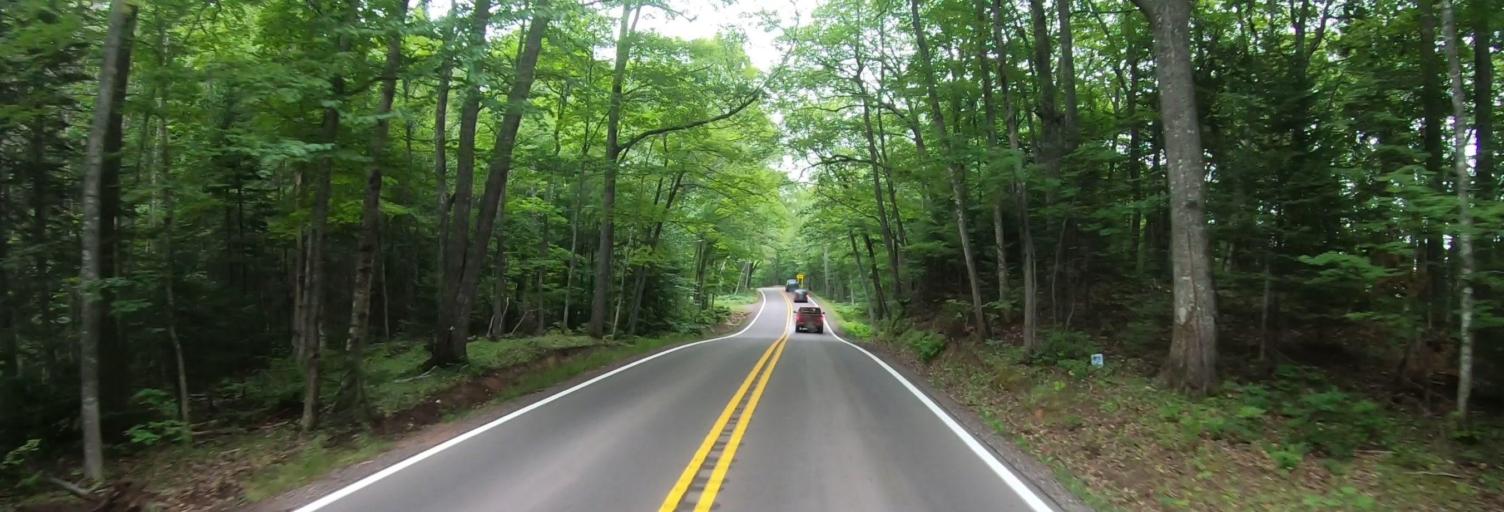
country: US
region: Michigan
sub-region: Keweenaw County
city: Eagle River
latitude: 47.4273
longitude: -87.9949
